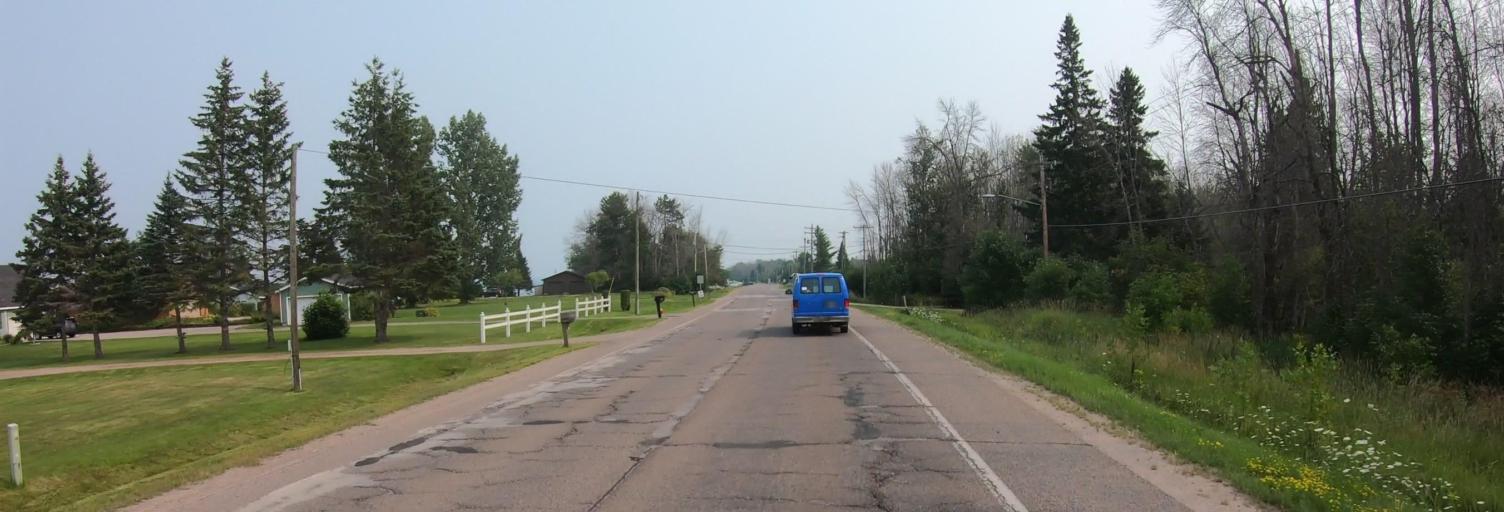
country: US
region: Michigan
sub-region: Chippewa County
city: Sault Ste. Marie
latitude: 46.4726
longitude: -84.3024
